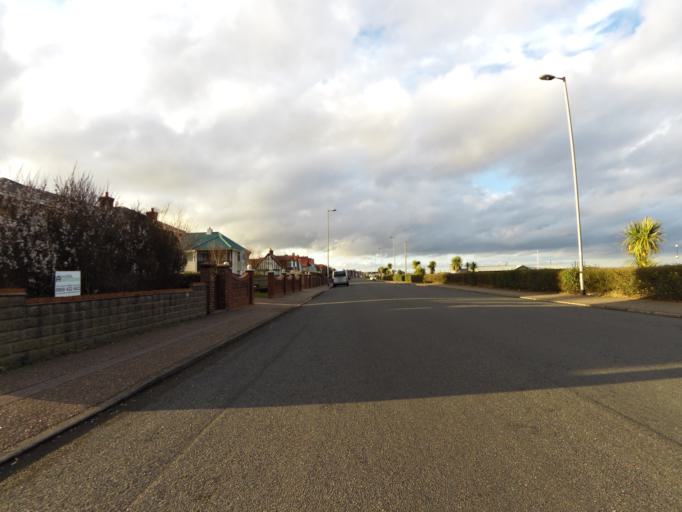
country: GB
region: England
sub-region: Norfolk
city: Gorleston-on-Sea
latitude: 52.5639
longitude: 1.7305
